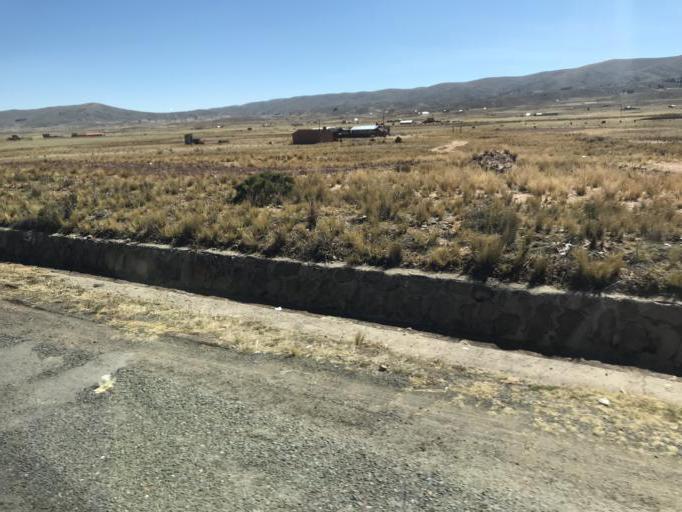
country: BO
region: La Paz
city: Tiahuanaco
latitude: -16.5939
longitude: -68.5789
